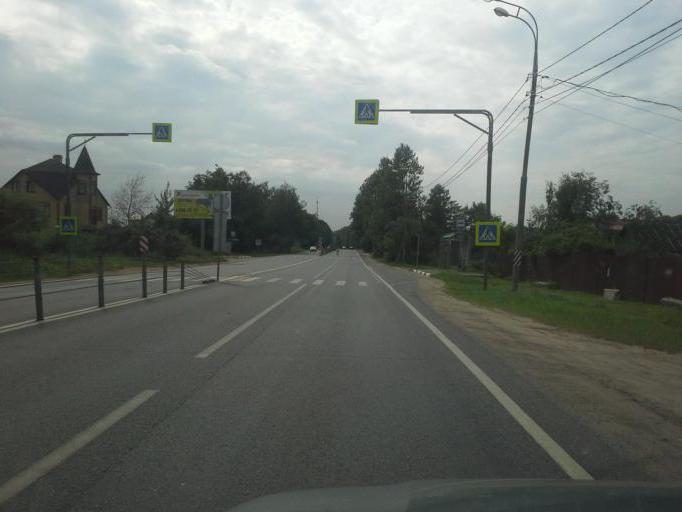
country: RU
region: Moskovskaya
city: Zhavoronki
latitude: 55.6584
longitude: 37.1276
